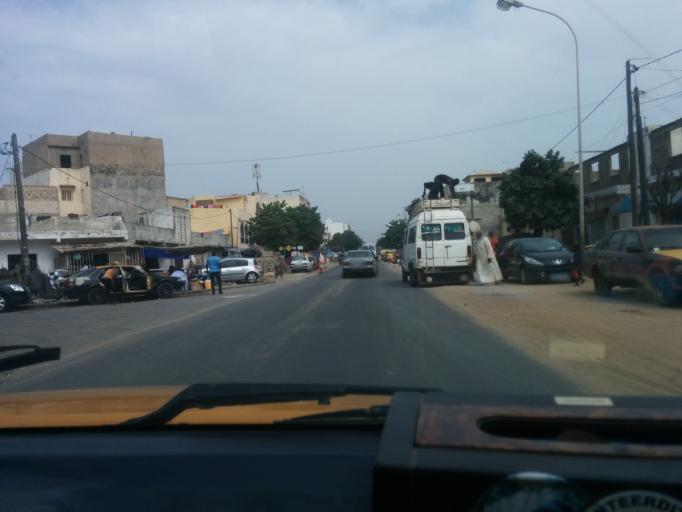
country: SN
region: Dakar
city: Grand Dakar
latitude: 14.7555
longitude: -17.4463
